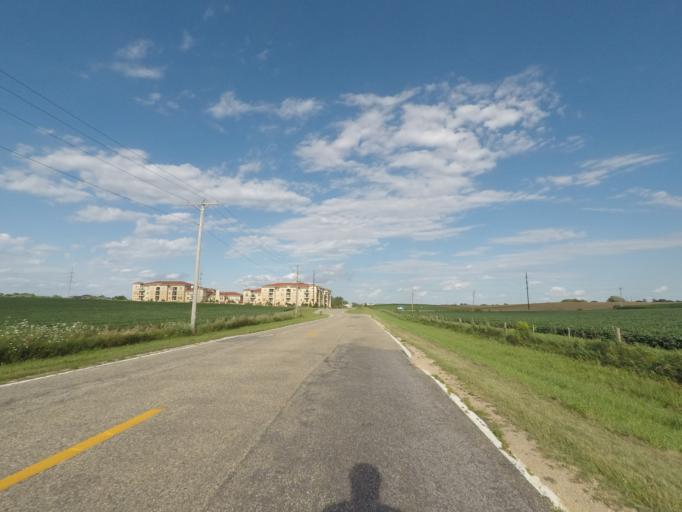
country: US
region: Wisconsin
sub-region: Dane County
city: Middleton
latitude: 43.0675
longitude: -89.5394
